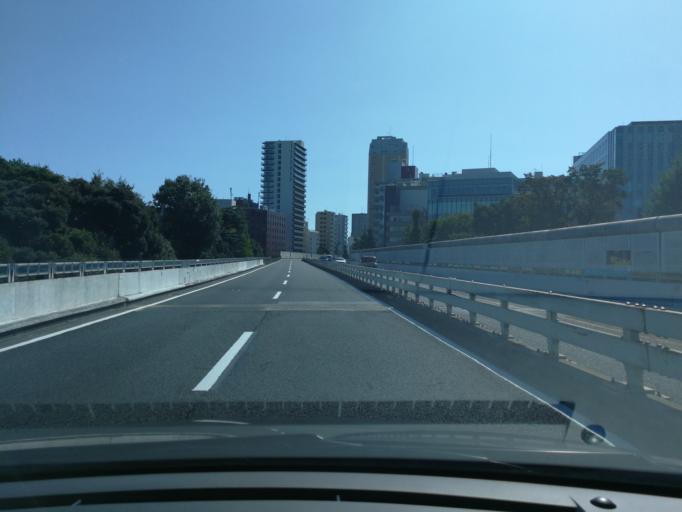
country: JP
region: Tokyo
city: Tokyo
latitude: 35.6364
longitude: 139.7179
